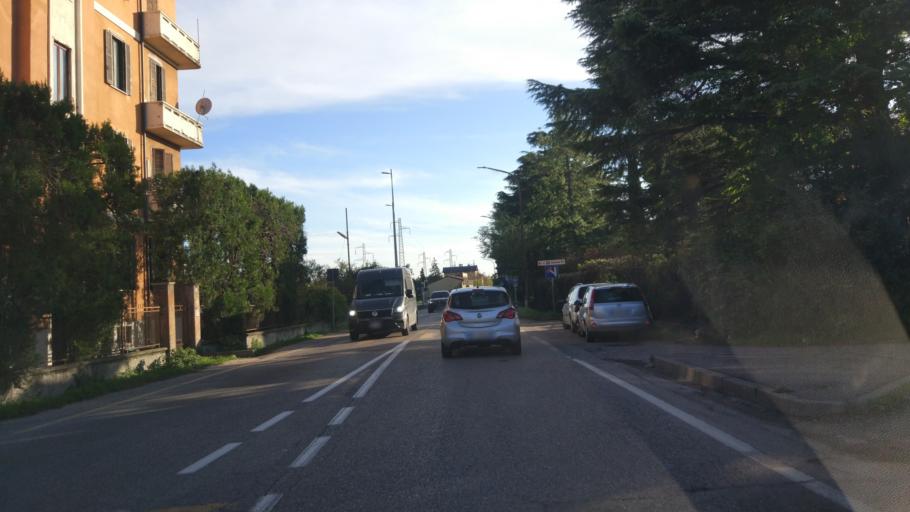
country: IT
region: Veneto
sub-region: Provincia di Verona
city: Volargne
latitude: 45.5230
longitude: 10.8184
